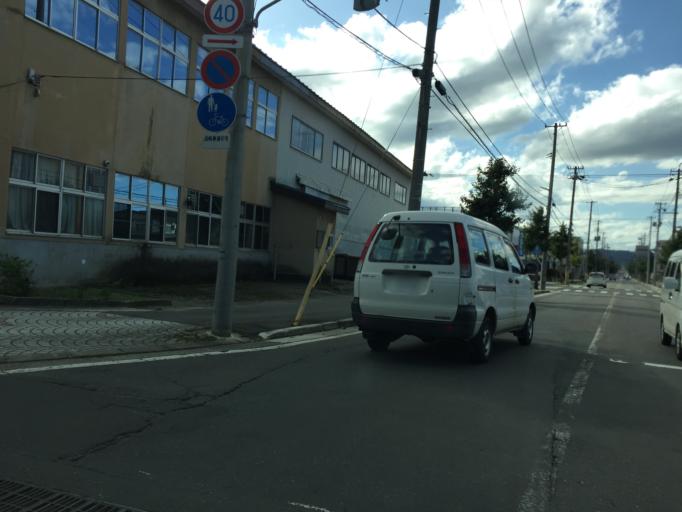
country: JP
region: Yamagata
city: Yonezawa
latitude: 37.9178
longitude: 140.1172
